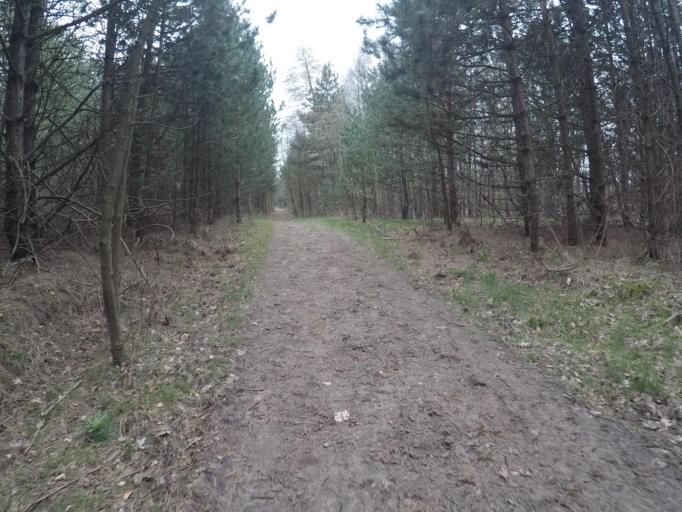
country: DE
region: Lower Saxony
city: Nordholz
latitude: 53.8117
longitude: 8.6354
